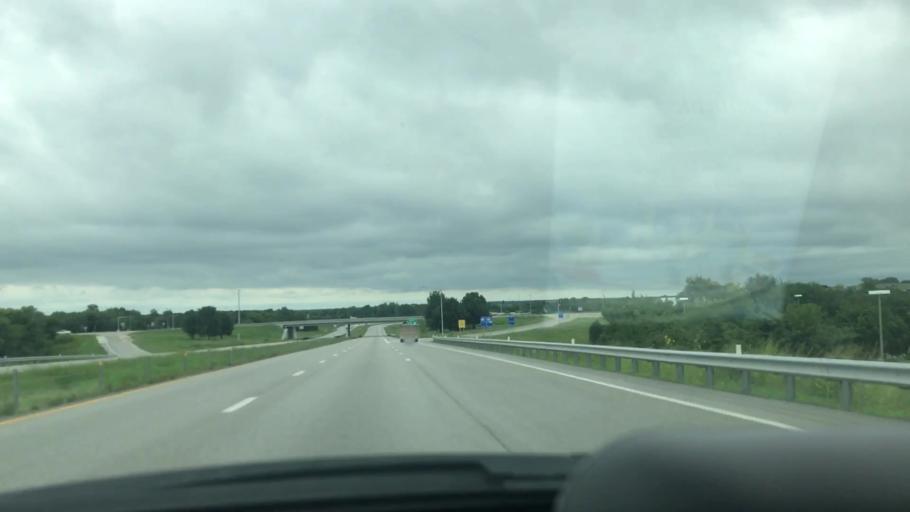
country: US
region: Missouri
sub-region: Greene County
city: Springfield
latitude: 37.2428
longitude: -93.3516
